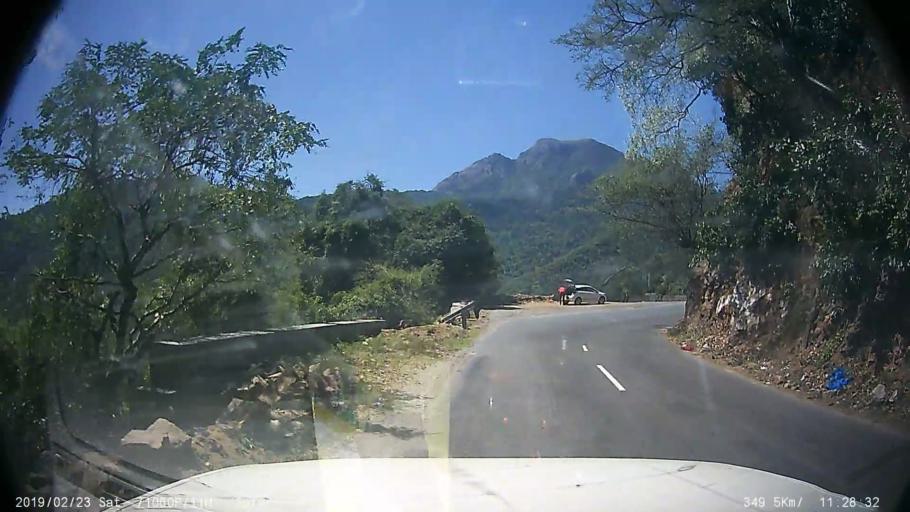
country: IN
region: Tamil Nadu
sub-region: Nilgiri
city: Kotagiri
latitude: 11.3404
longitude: 76.8643
